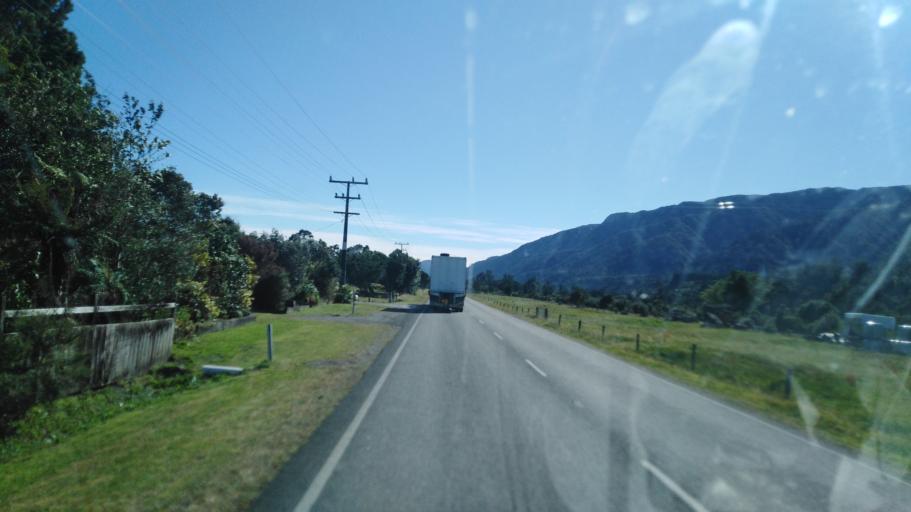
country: NZ
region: West Coast
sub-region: Buller District
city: Westport
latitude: -41.6746
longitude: 171.8001
